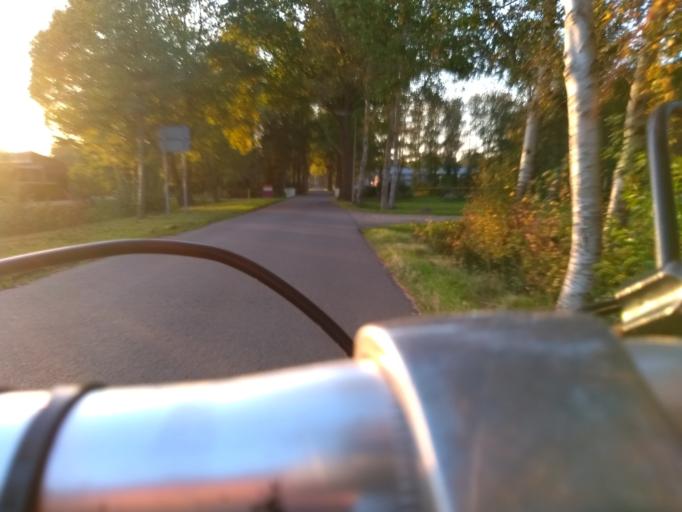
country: NL
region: Drenthe
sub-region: Gemeente Assen
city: Assen
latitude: 52.9779
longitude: 6.5728
